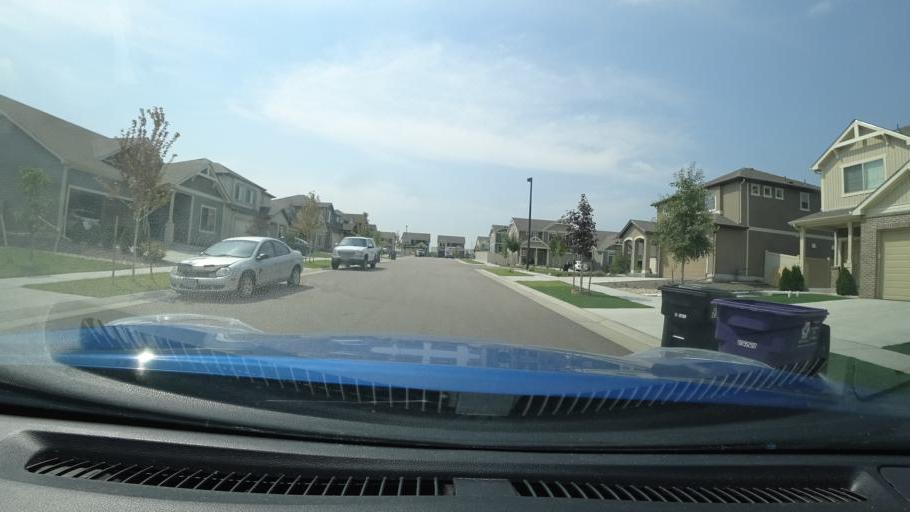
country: US
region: Colorado
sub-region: Adams County
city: Aurora
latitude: 39.7776
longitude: -104.7803
